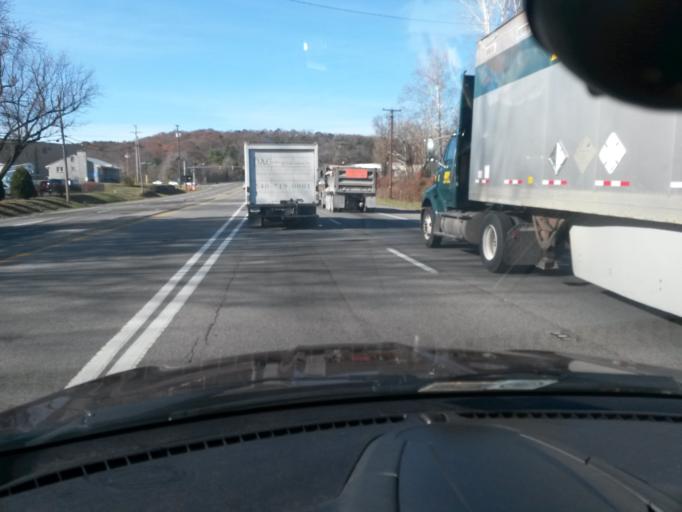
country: US
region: Virginia
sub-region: Roanoke County
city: Narrows
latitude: 37.2039
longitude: -79.9509
